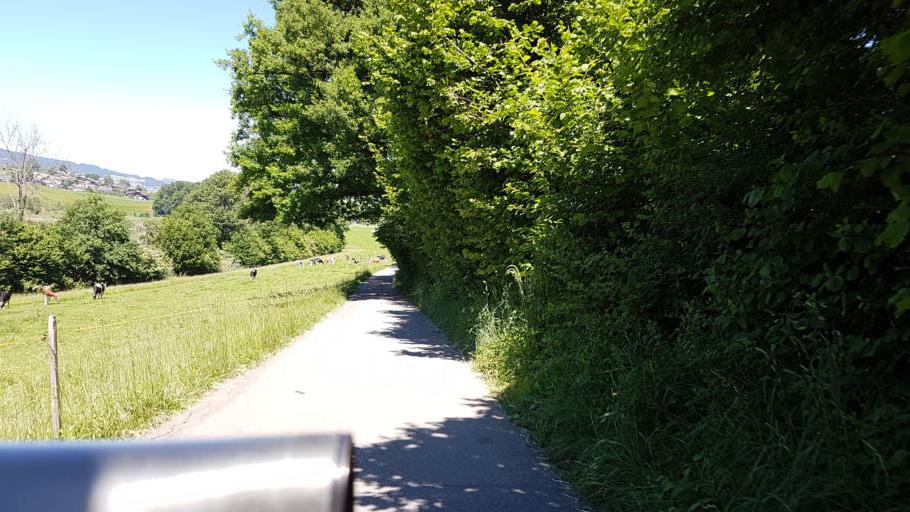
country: CH
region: Bern
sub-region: Thun District
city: Thierachern
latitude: 46.7334
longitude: 7.5688
